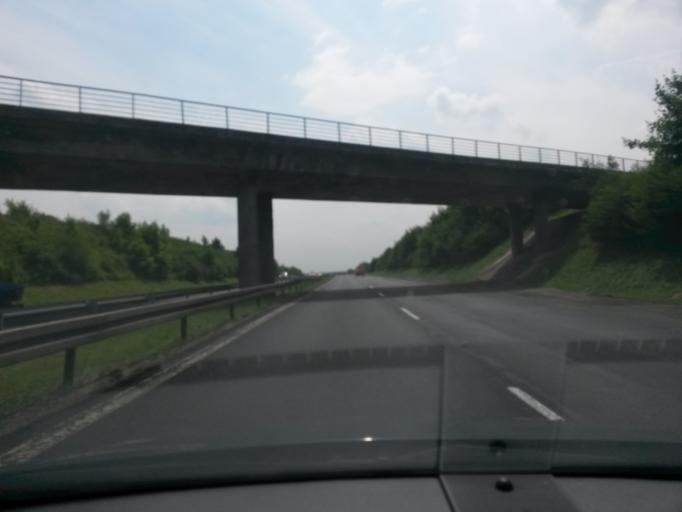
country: PL
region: Lodz Voivodeship
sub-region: Powiat radomszczanski
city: Kamiensk
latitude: 51.1942
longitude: 19.4739
